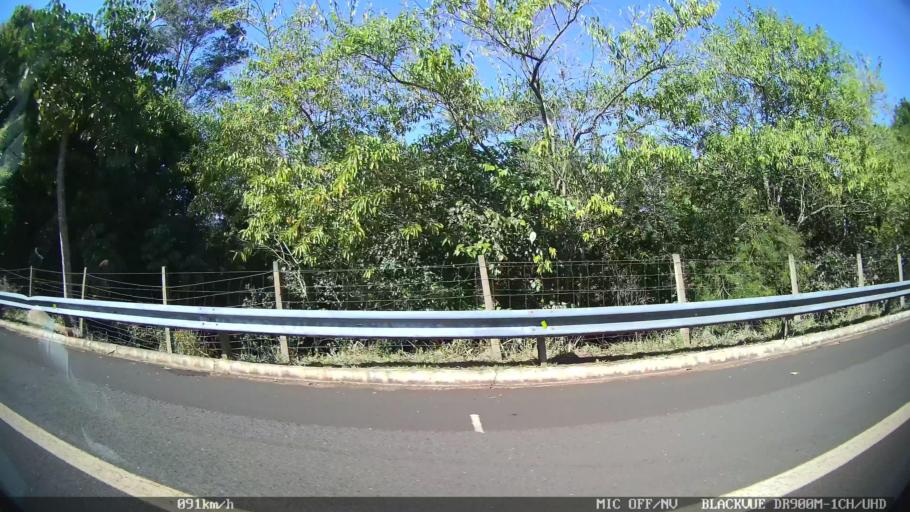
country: BR
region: Sao Paulo
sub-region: Batatais
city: Batatais
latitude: -20.7290
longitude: -47.5209
